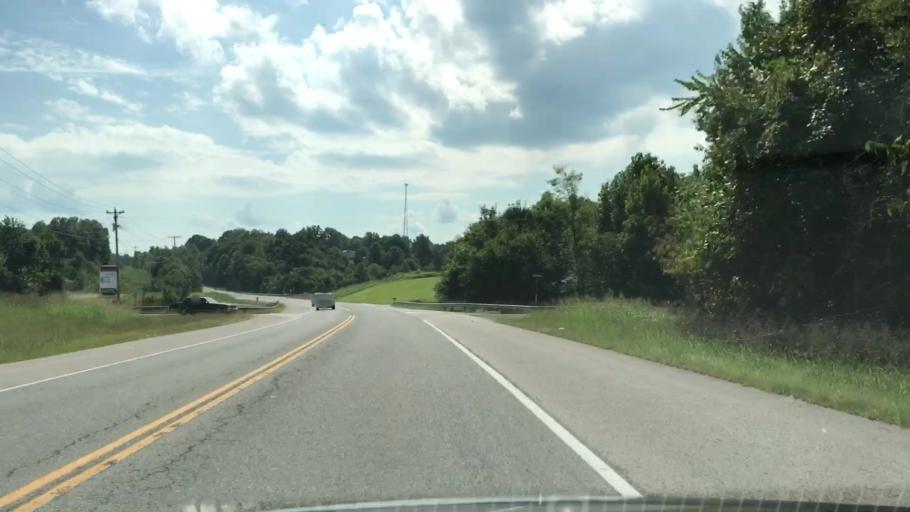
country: US
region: Tennessee
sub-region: Sumner County
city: Westmoreland
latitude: 36.5461
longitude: -86.2194
